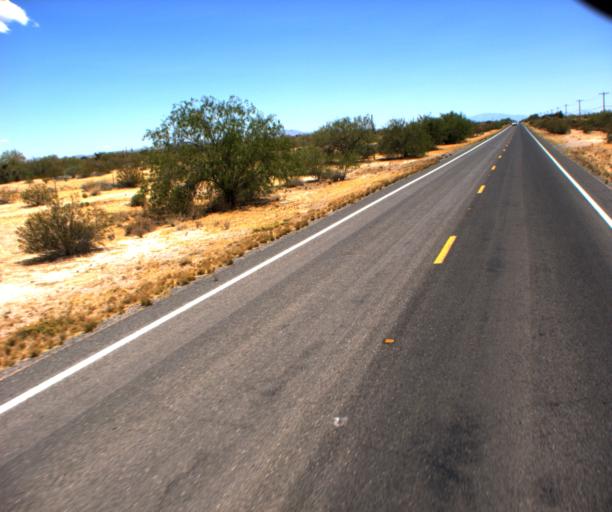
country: US
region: Arizona
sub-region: Pinal County
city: Florence
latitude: 32.9550
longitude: -111.3302
